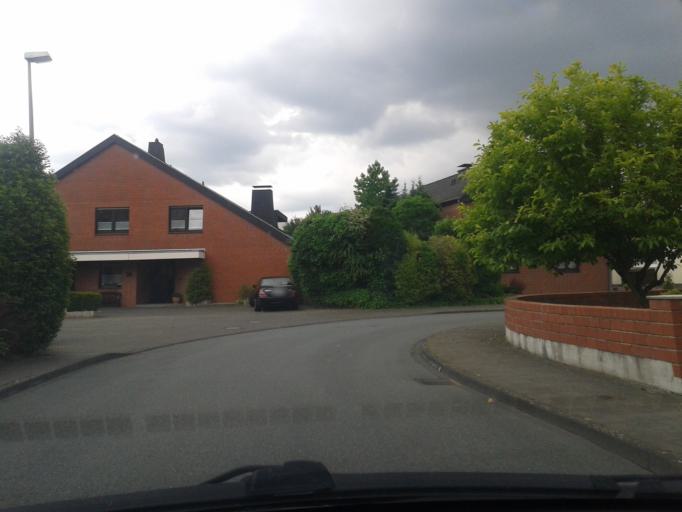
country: DE
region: North Rhine-Westphalia
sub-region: Regierungsbezirk Detmold
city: Paderborn
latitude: 51.7275
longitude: 8.7313
